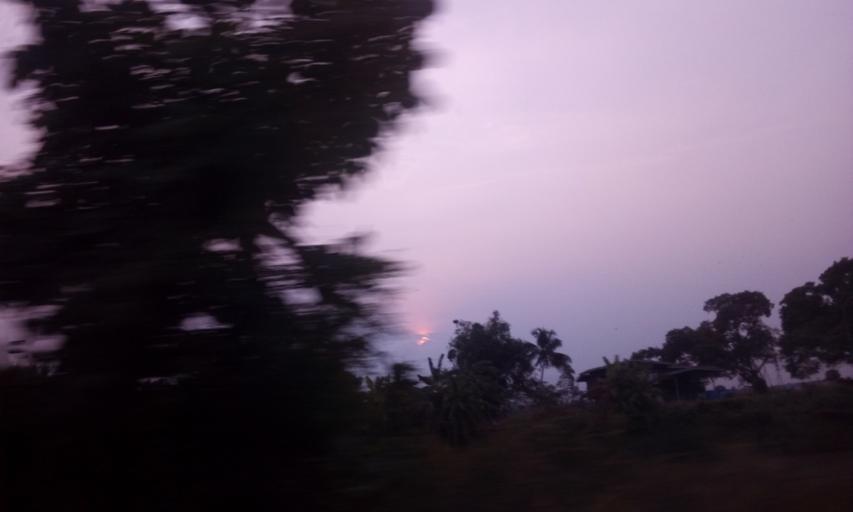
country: TH
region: Pathum Thani
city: Nong Suea
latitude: 14.0347
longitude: 100.8937
